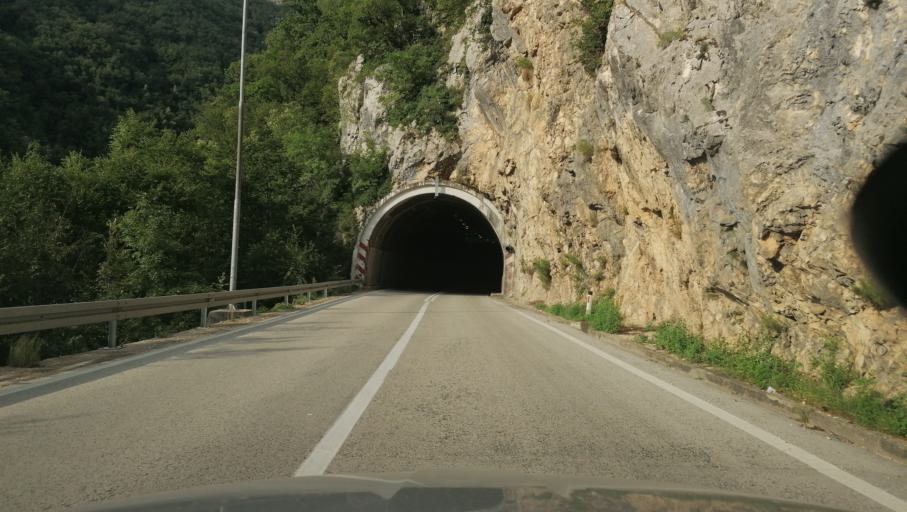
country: BA
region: Federation of Bosnia and Herzegovina
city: Jajce
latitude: 44.4627
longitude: 17.2260
